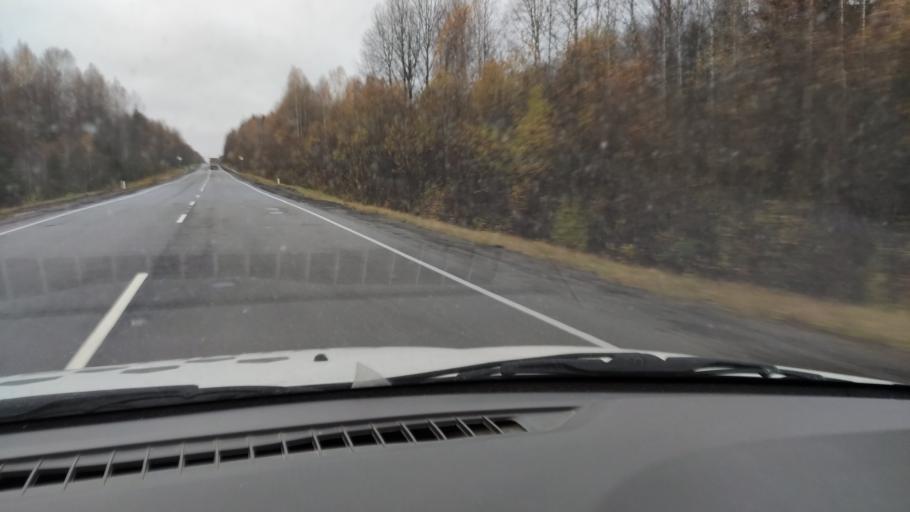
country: RU
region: Kirov
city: Omutninsk
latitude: 58.7629
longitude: 51.9985
